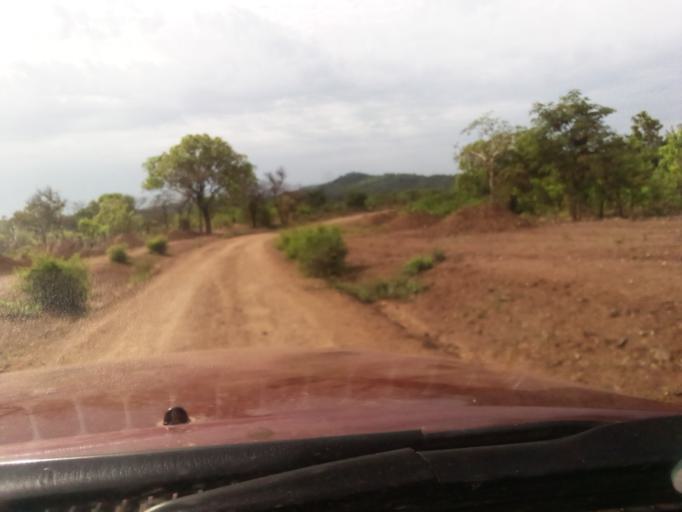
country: ET
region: Oromiya
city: Mendi
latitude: 10.0438
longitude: 35.3046
